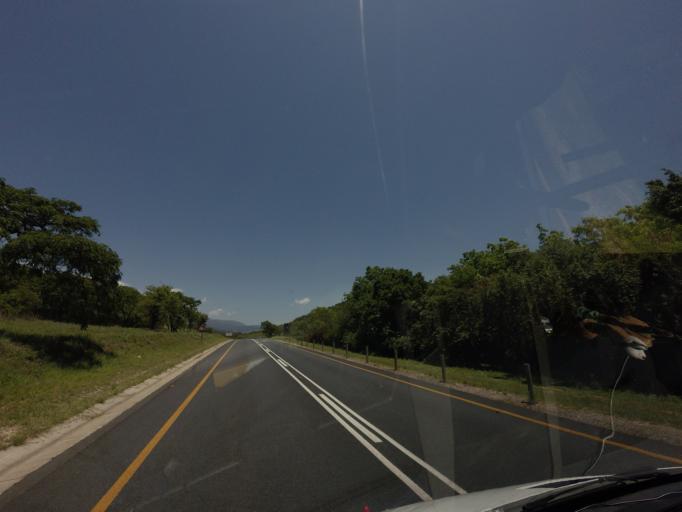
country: ZA
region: Mpumalanga
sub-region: Ehlanzeni District
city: Nelspruit
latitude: -25.4513
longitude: 30.7055
